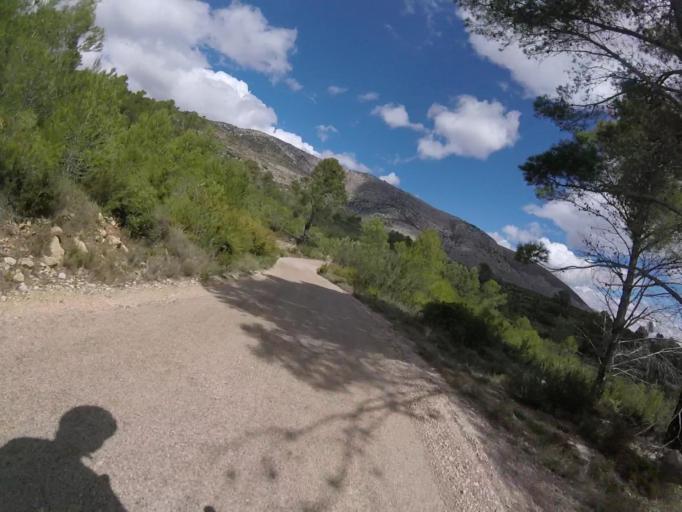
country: ES
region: Valencia
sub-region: Provincia de Castello
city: Sierra-Engarceran
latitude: 40.2852
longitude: -0.0698
